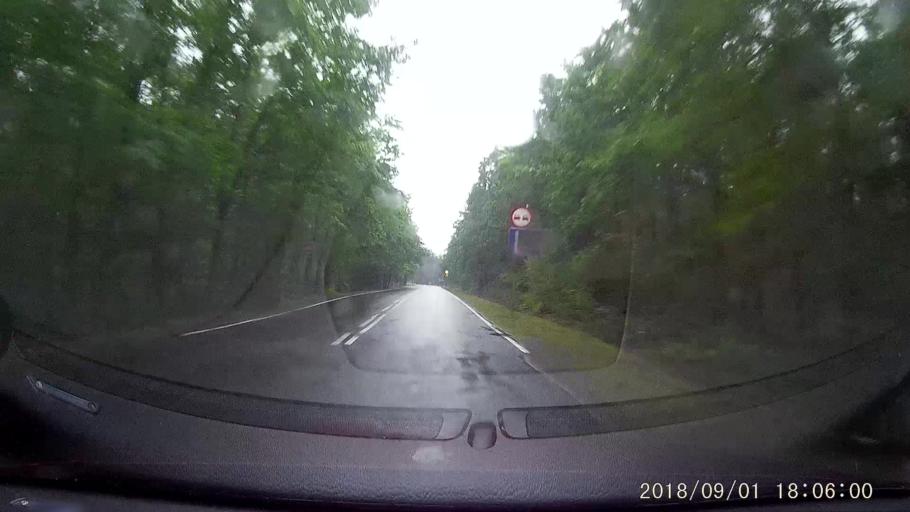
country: PL
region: Lubusz
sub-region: Powiat zaganski
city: Gozdnica
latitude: 51.3587
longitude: 15.1587
